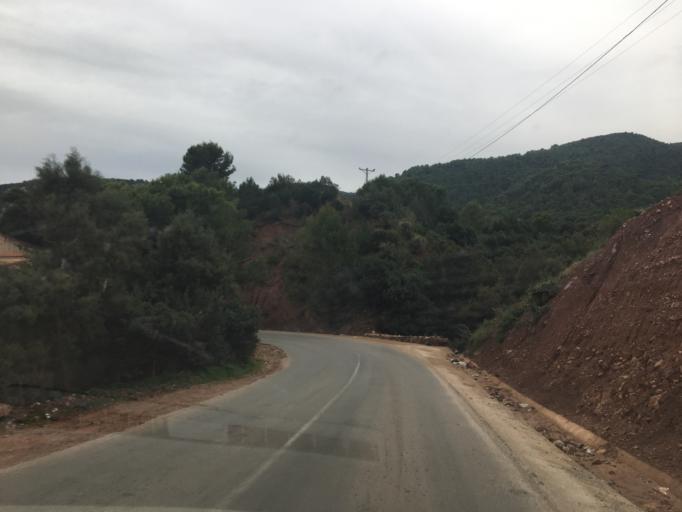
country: DZ
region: Tipaza
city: Tipasa
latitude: 36.6286
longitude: 2.4006
